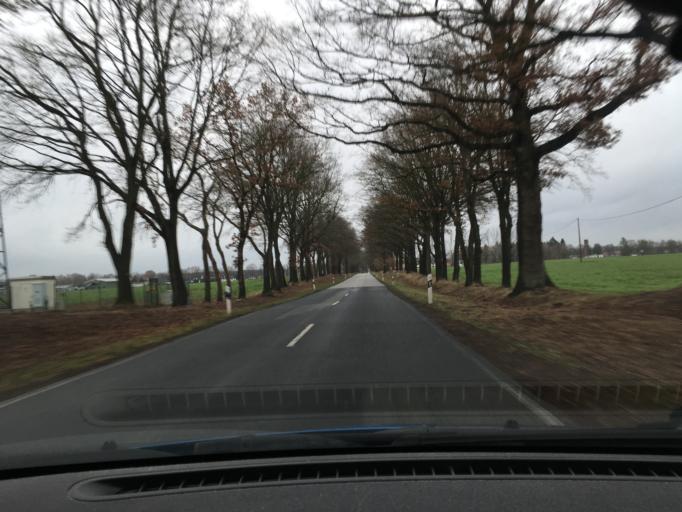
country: DE
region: Mecklenburg-Vorpommern
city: Nostorf
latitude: 53.4232
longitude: 10.6837
